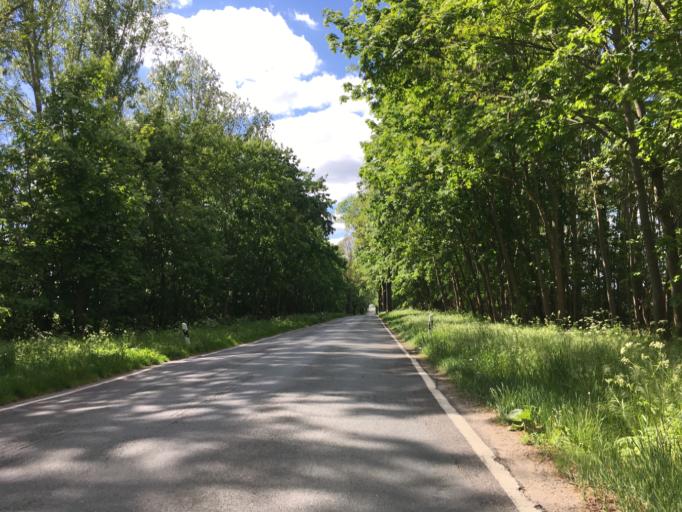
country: DE
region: Brandenburg
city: Rudnitz
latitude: 52.6651
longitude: 13.6662
